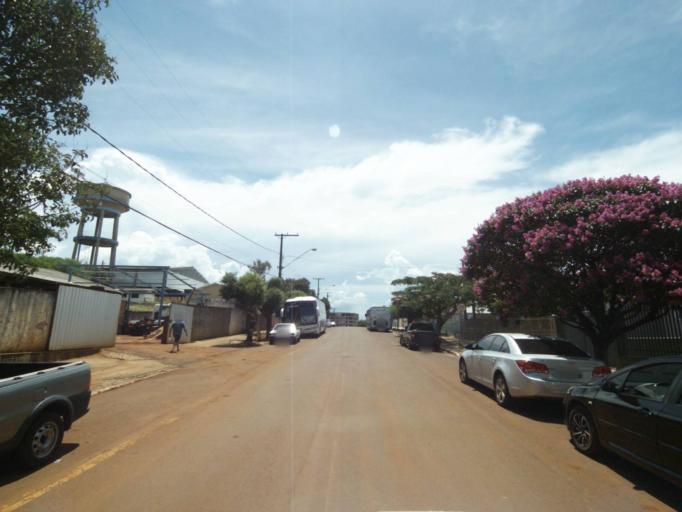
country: BR
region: Parana
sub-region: Guaraniacu
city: Guaraniacu
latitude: -25.0998
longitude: -52.8658
